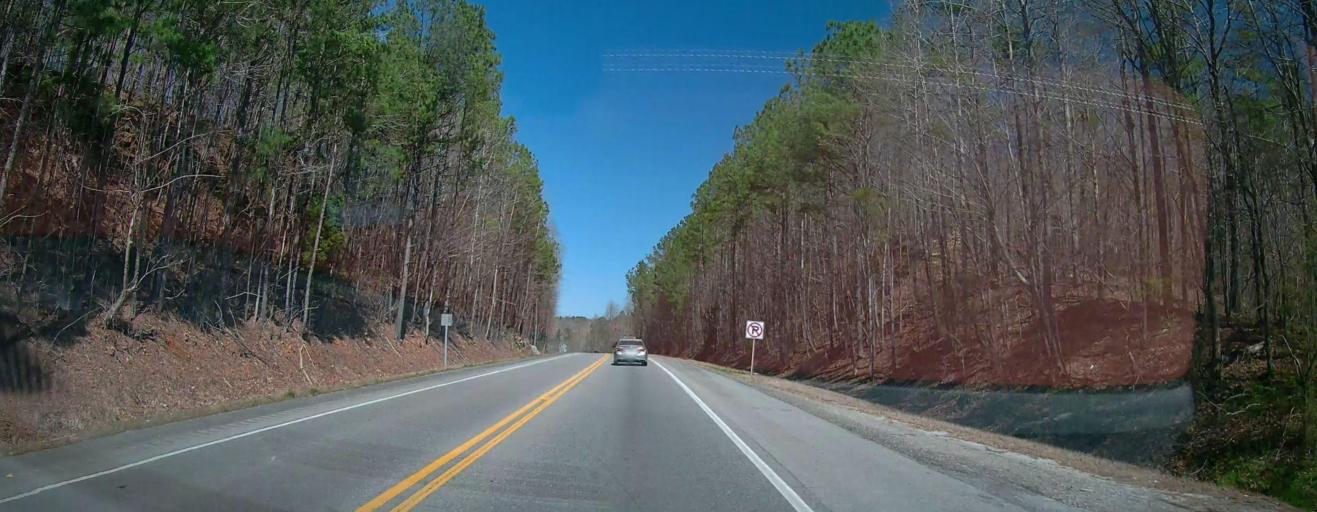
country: US
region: Alabama
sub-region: Calhoun County
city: Ohatchee
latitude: 33.7862
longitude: -86.0359
